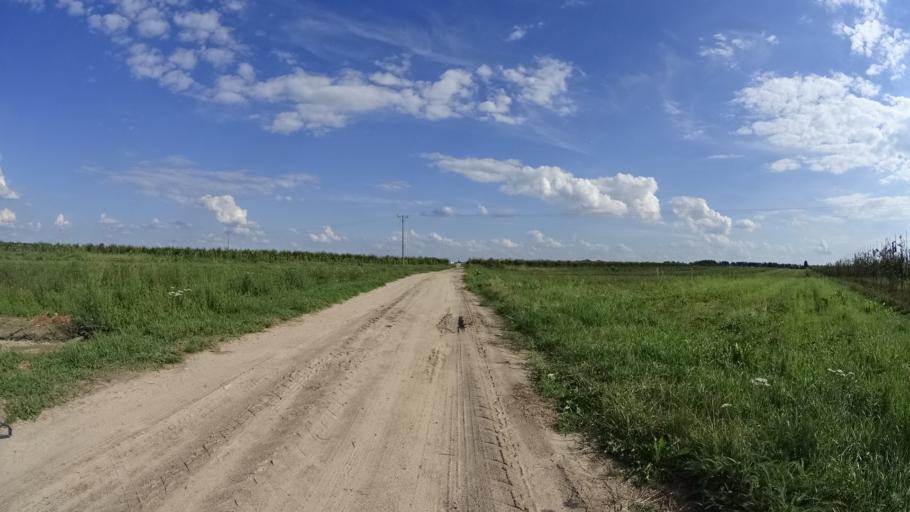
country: PL
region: Masovian Voivodeship
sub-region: Powiat bialobrzeski
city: Wysmierzyce
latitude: 51.6638
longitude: 20.8155
